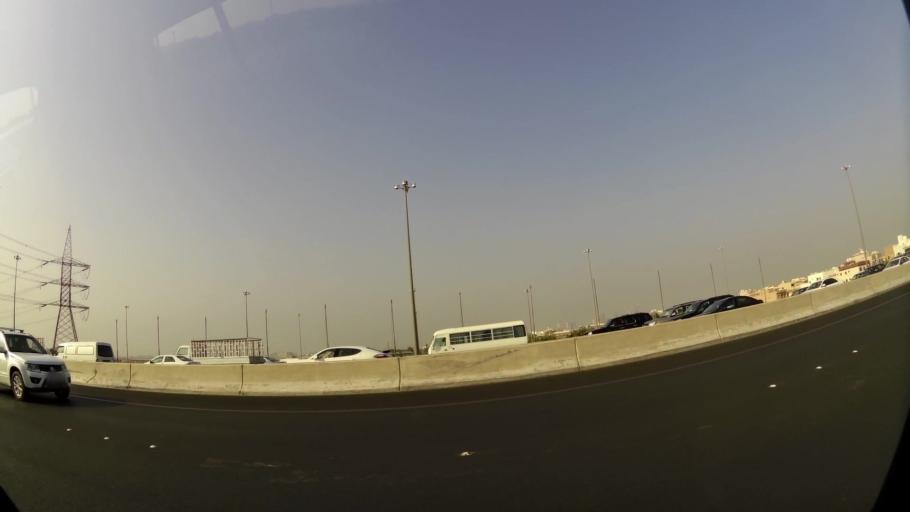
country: KW
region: Al Farwaniyah
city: Al Farwaniyah
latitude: 29.3028
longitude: 47.9637
